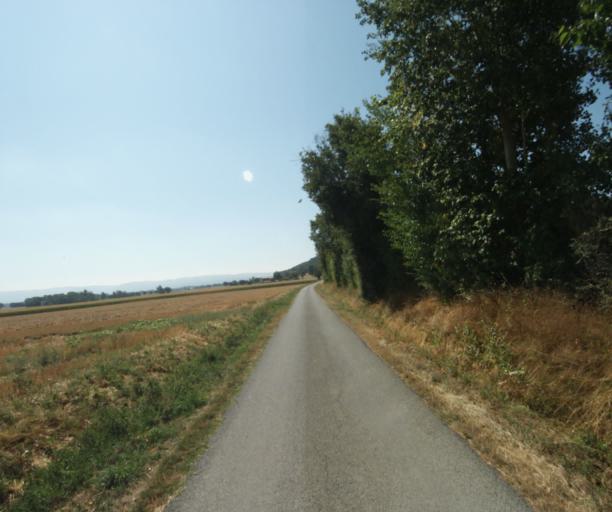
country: FR
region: Midi-Pyrenees
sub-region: Departement du Tarn
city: Puylaurens
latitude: 43.5247
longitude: 1.9414
